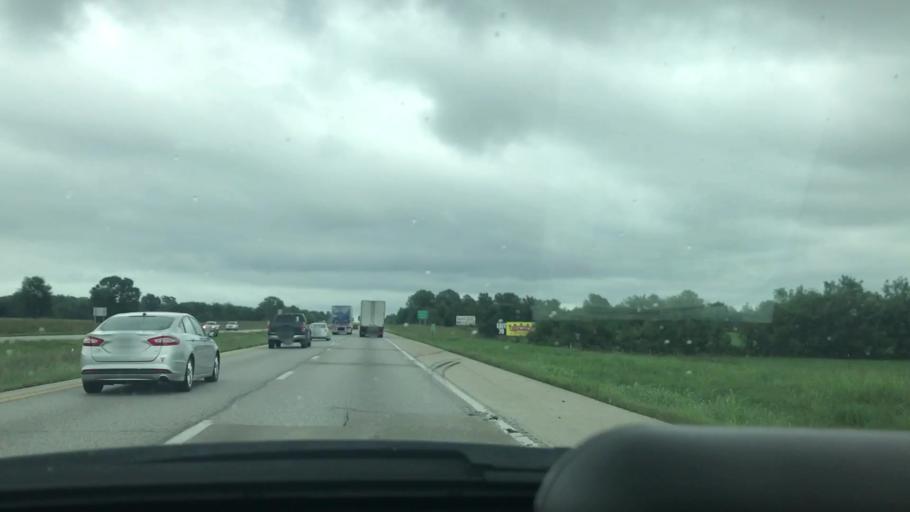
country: US
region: Missouri
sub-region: Greene County
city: Ash Grove
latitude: 37.1868
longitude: -93.6086
